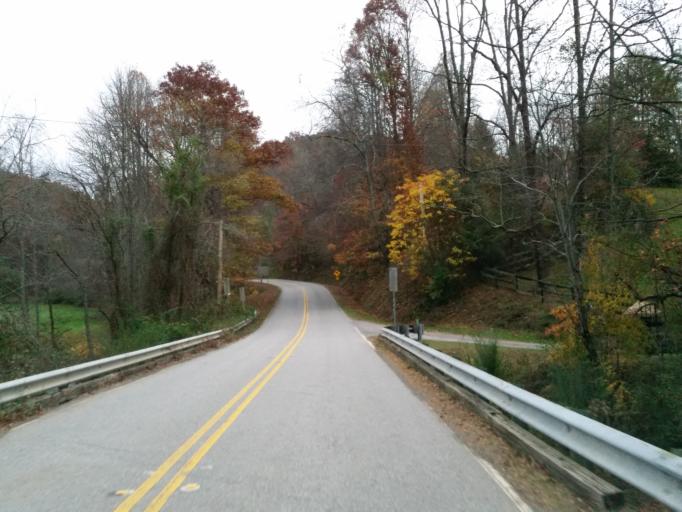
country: US
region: Georgia
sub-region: Lumpkin County
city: Dahlonega
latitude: 34.7041
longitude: -84.0557
